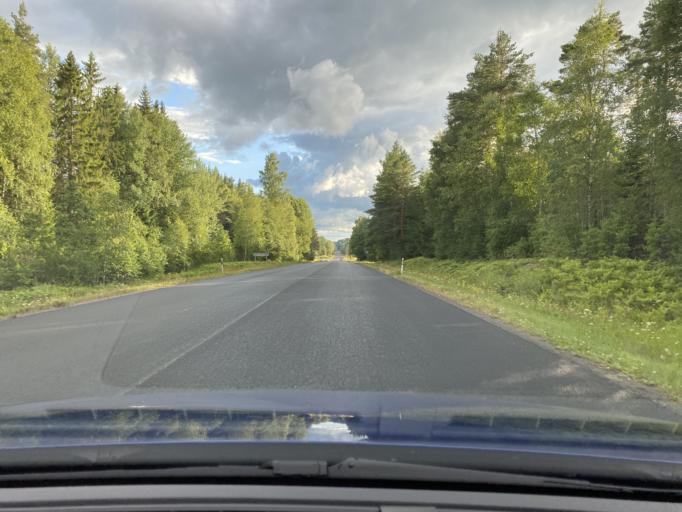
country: FI
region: Haeme
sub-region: Haemeenlinna
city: Renko
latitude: 60.9038
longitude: 24.2966
